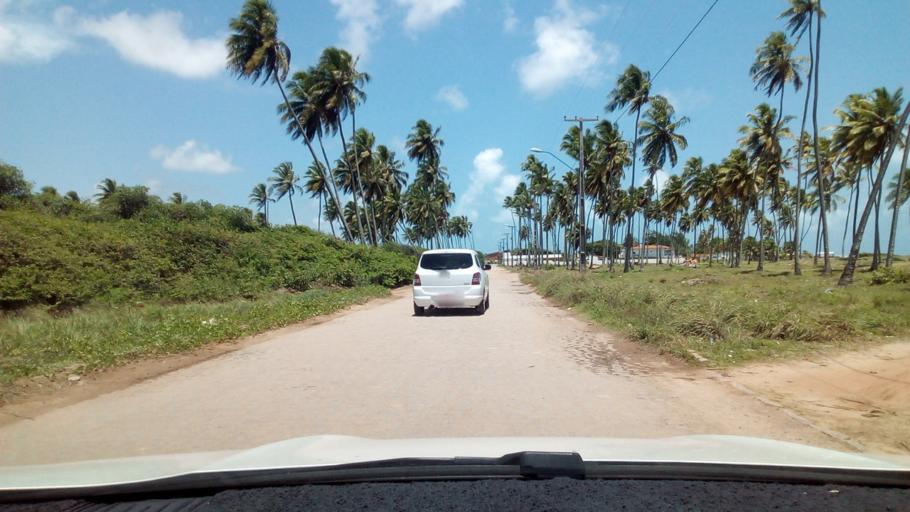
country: BR
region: Paraiba
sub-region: Pitimbu
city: Pitimbu
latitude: -7.5286
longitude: -34.8206
